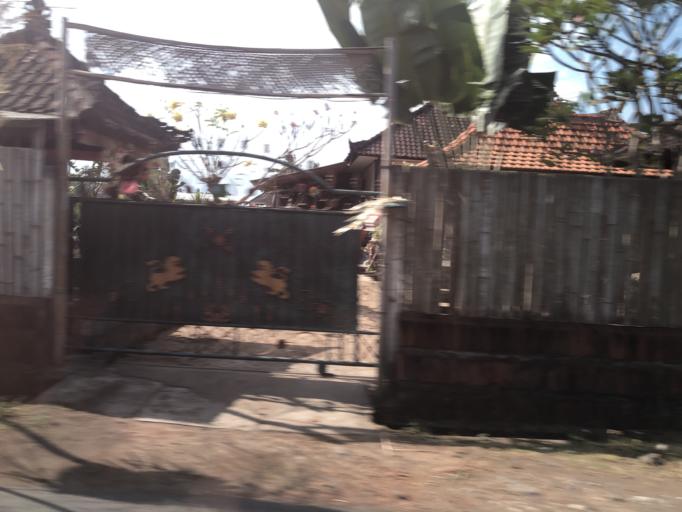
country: ID
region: Bali
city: Banjar Bucu
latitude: -8.5779
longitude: 115.2033
